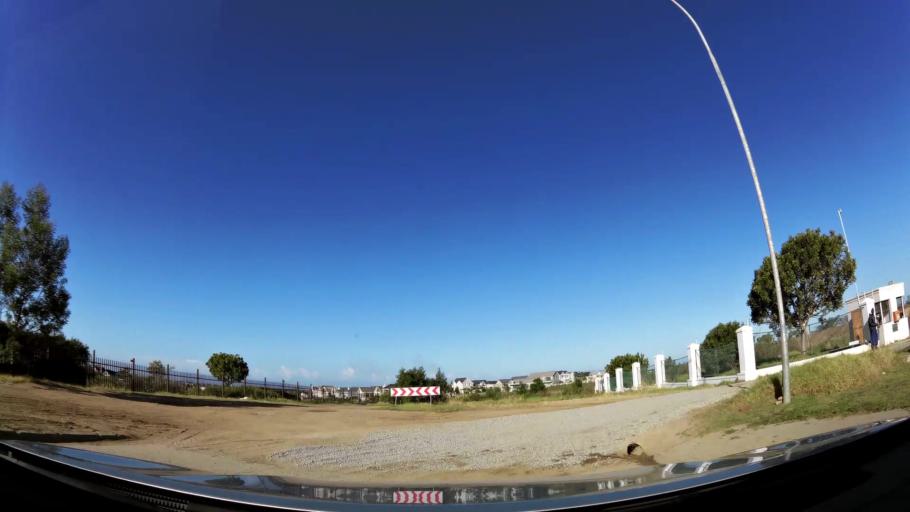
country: ZA
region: Western Cape
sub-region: Eden District Municipality
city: George
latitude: -33.9686
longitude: 22.4286
